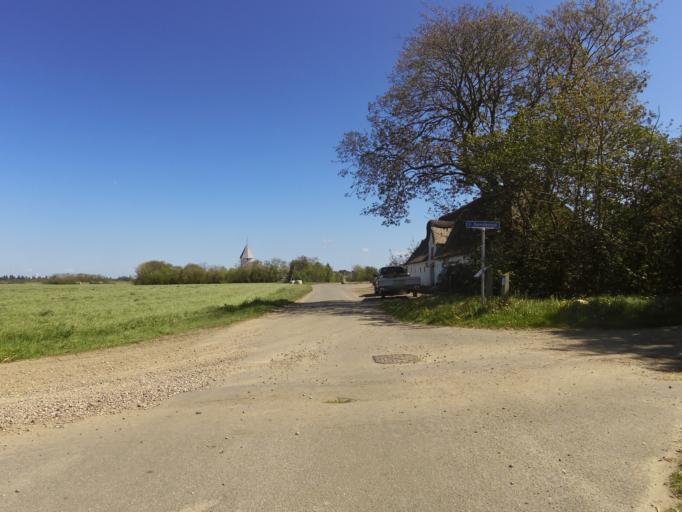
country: DK
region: South Denmark
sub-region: Tonder Kommune
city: Sherrebek
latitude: 55.2379
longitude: 8.7100
